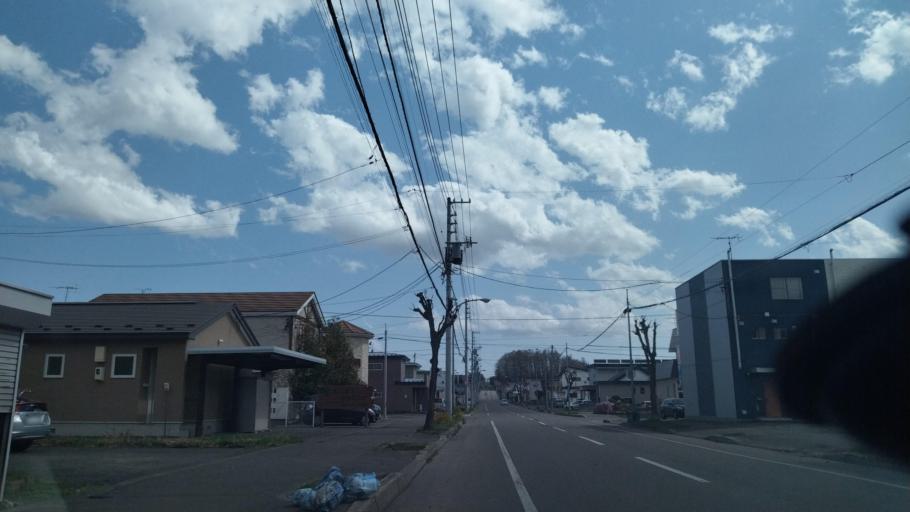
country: JP
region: Hokkaido
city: Obihiro
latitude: 42.9064
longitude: 143.1528
